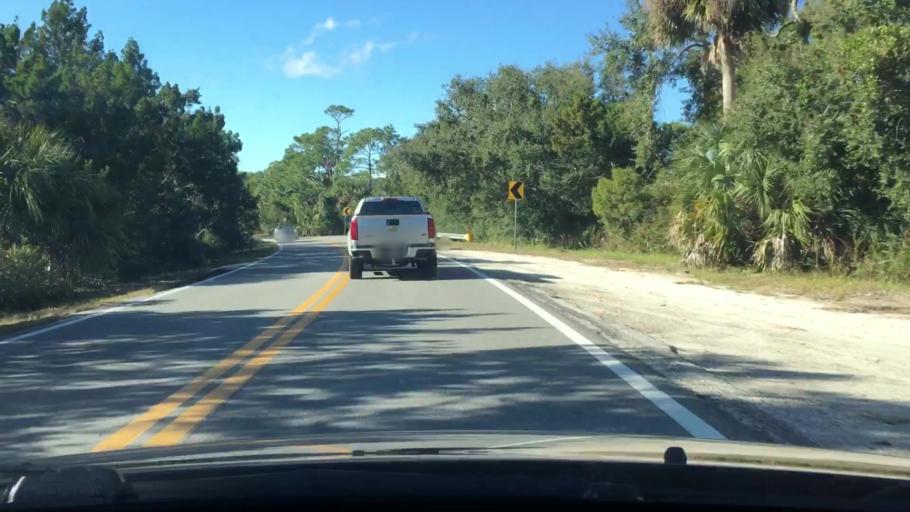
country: US
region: Florida
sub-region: Volusia County
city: Ormond-by-the-Sea
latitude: 29.3532
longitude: -81.1019
